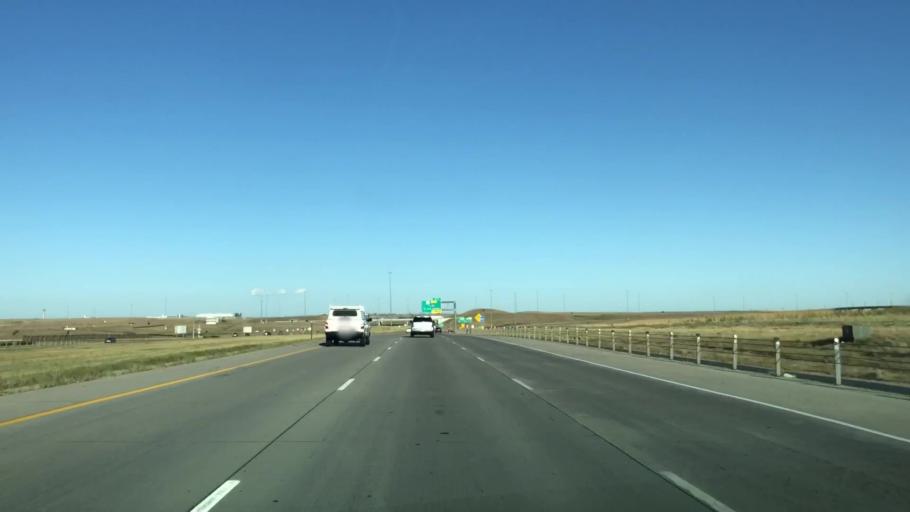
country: US
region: Colorado
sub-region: Adams County
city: Aurora
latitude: 39.8339
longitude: -104.7621
